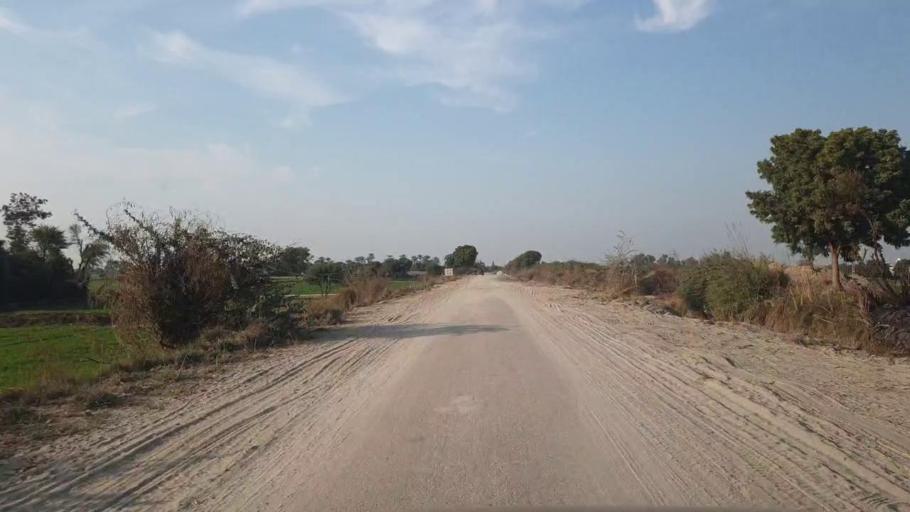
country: PK
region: Sindh
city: Shahpur Chakar
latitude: 26.1505
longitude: 68.6425
